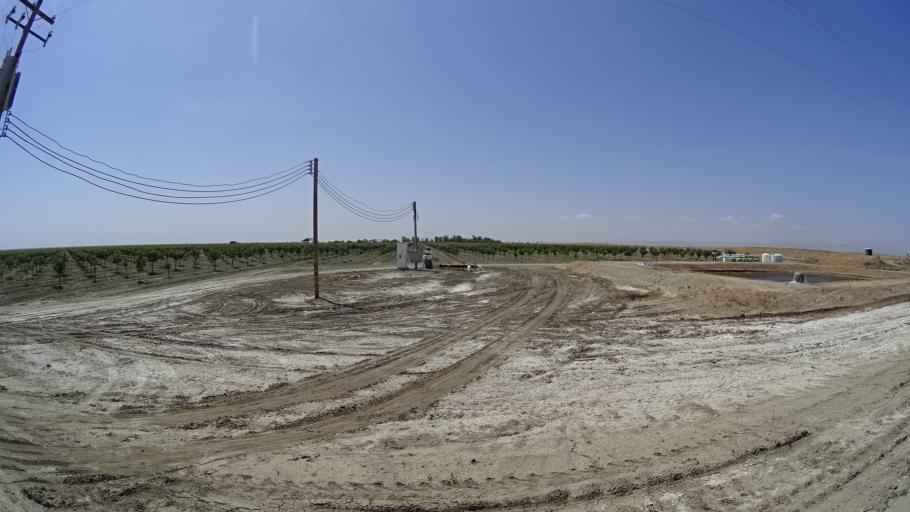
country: US
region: California
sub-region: Kings County
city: Stratford
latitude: 36.1379
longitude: -119.8865
